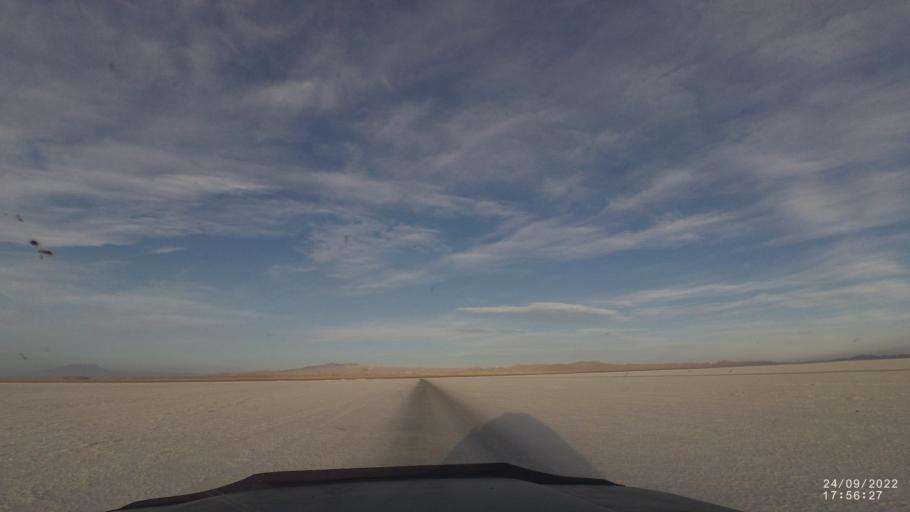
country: BO
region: Potosi
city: Colchani
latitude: -20.3240
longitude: -67.0123
